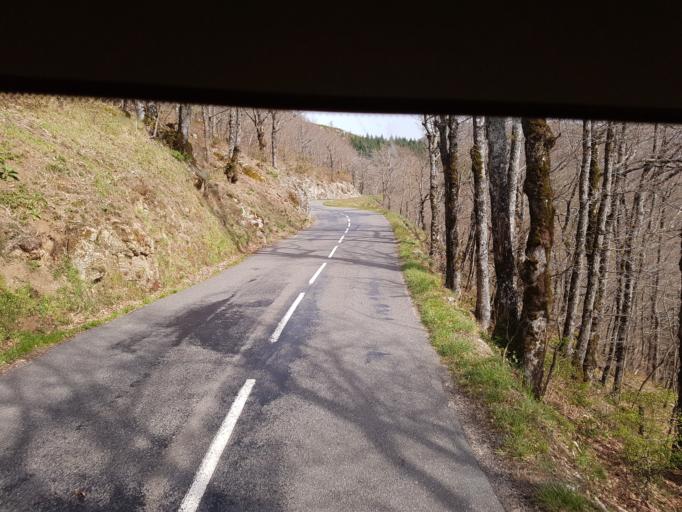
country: FR
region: Languedoc-Roussillon
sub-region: Departement de la Lozere
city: Florac
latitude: 44.3638
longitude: 3.7094
